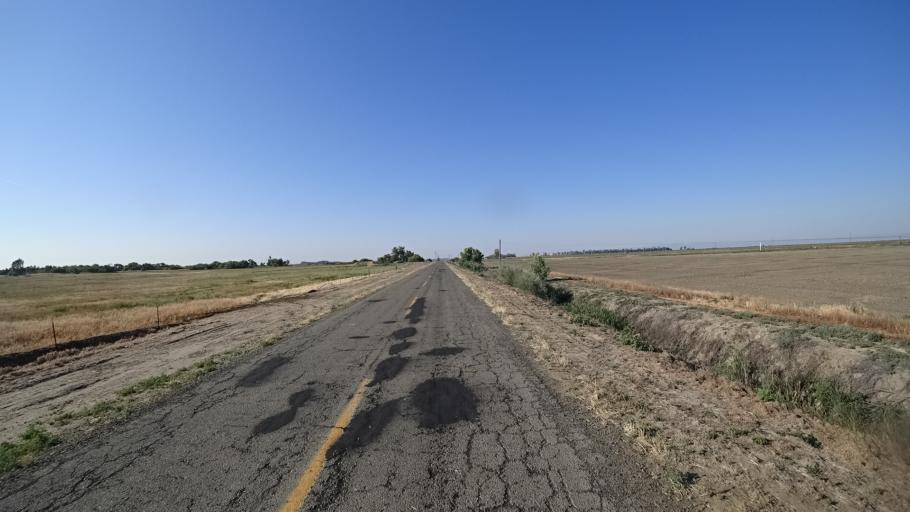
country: US
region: California
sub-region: Fresno County
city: Riverdale
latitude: 36.3944
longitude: -119.9277
